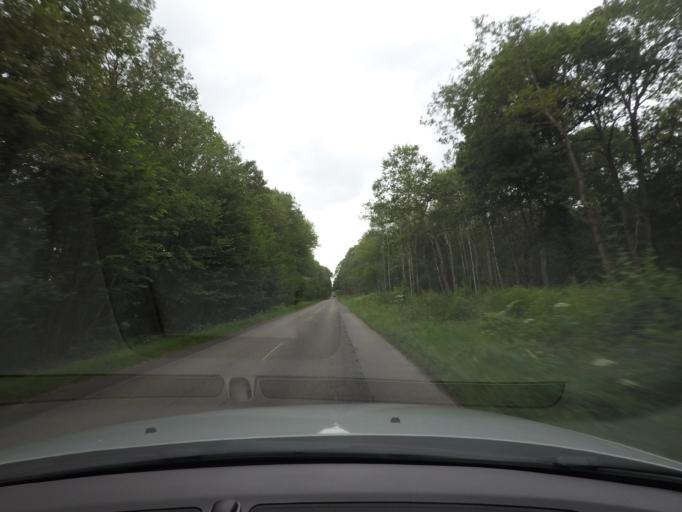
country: FR
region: Haute-Normandie
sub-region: Departement de l'Eure
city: Le Manoir
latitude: 49.3327
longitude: 1.2036
